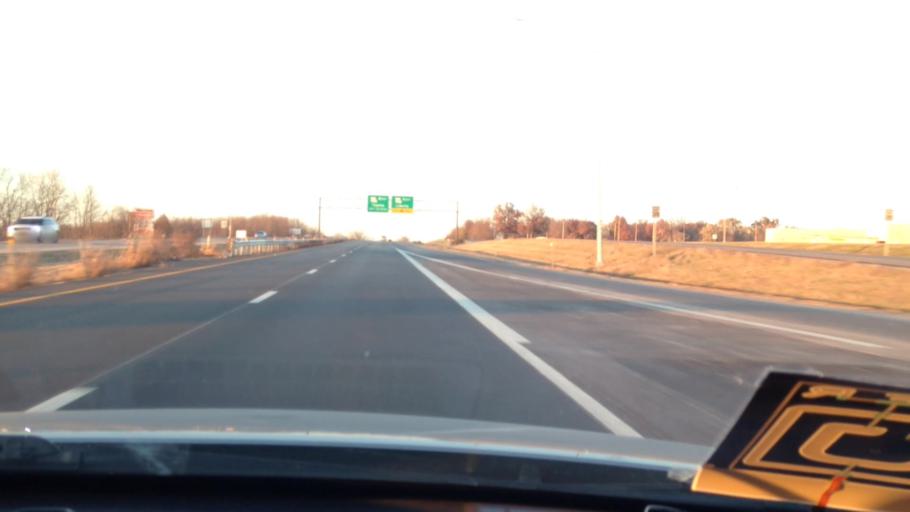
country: US
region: Missouri
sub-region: Clay County
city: Gladstone
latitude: 39.2483
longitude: -94.5902
